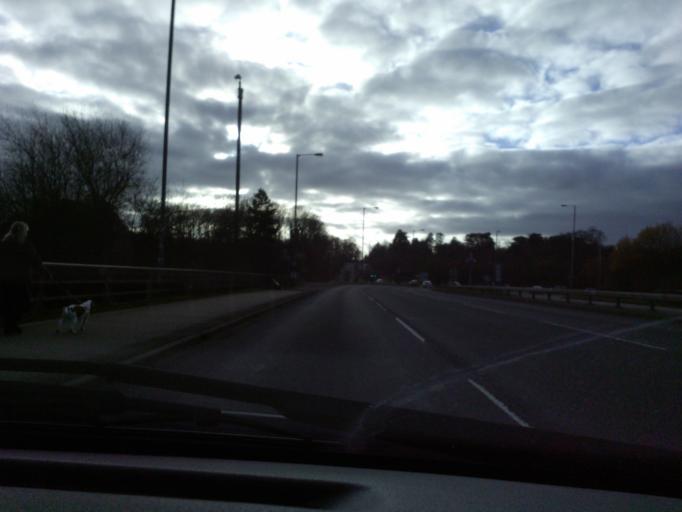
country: GB
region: England
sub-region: Hampshire
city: Totton
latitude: 50.9036
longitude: -1.5009
